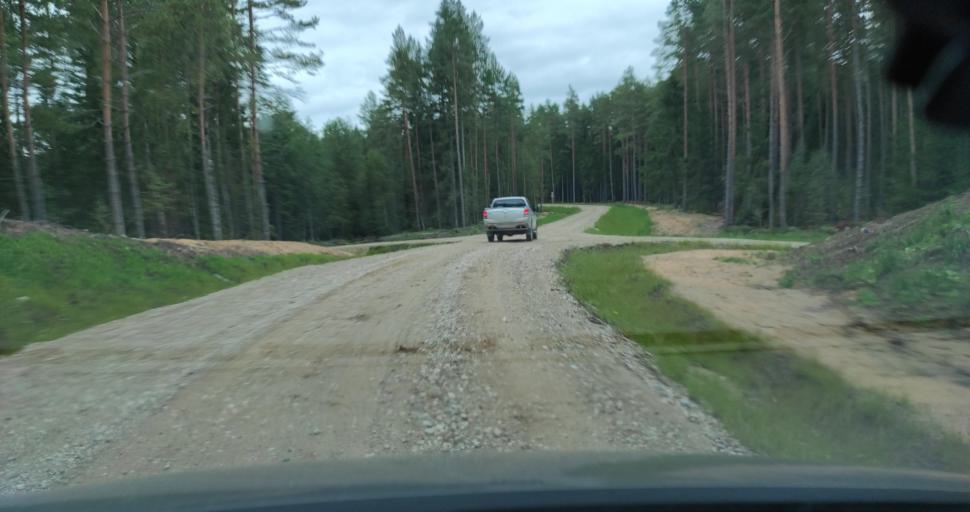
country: LV
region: Kuldigas Rajons
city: Kuldiga
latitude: 57.0870
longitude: 22.2178
